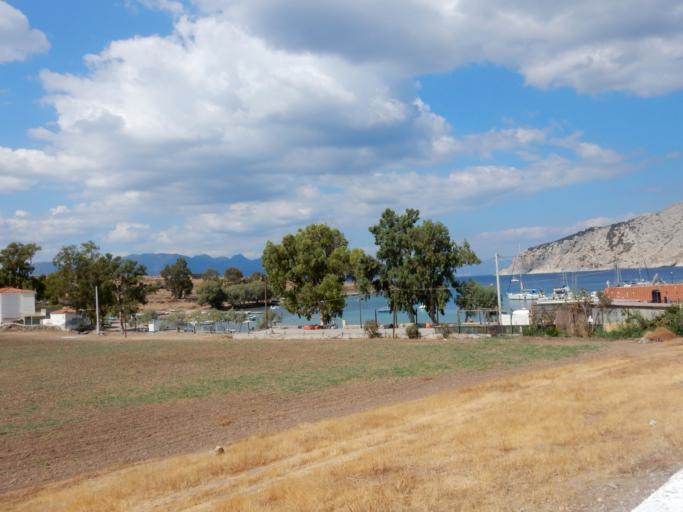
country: GR
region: Attica
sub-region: Nomos Piraios
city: Aegina
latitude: 37.6909
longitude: 23.4550
